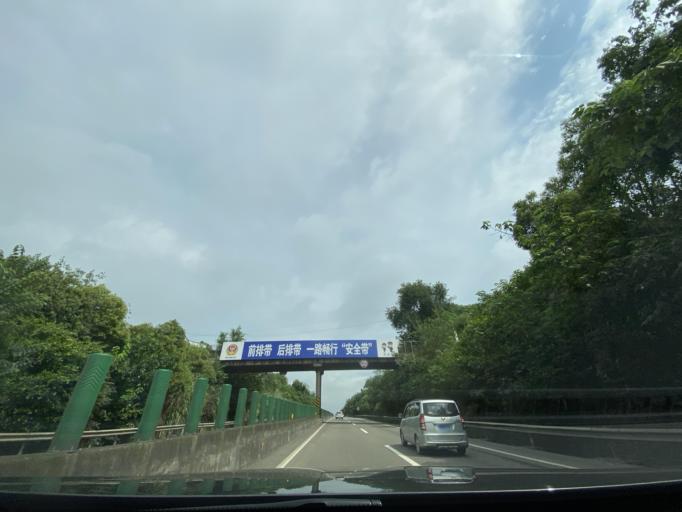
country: CN
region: Sichuan
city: Chonglong
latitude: 29.7303
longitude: 104.9176
